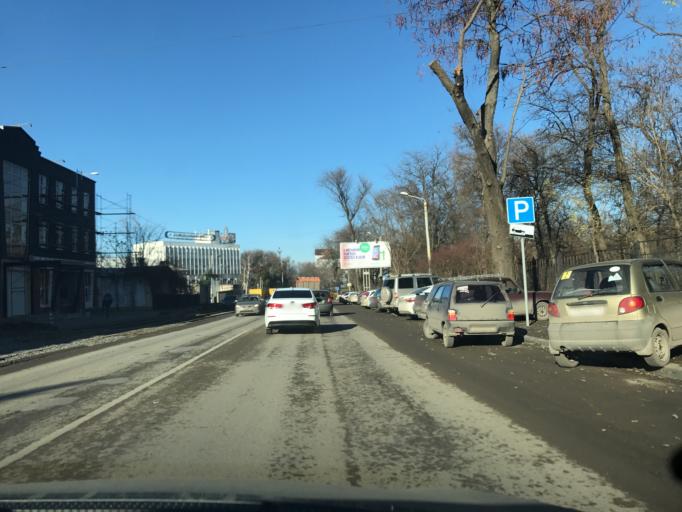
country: RU
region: Rostov
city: Rostov-na-Donu
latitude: 47.2415
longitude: 39.7523
